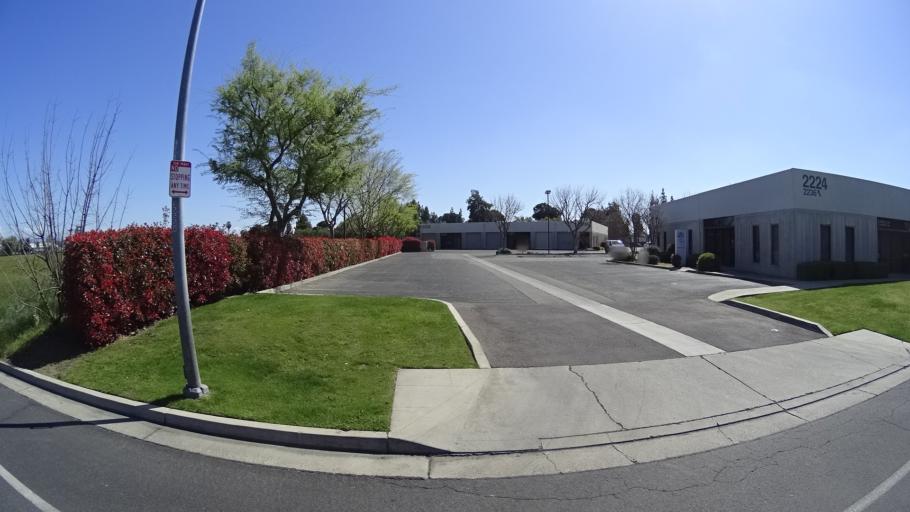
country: US
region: California
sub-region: Fresno County
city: Tarpey Village
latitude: 36.7707
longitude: -119.7270
